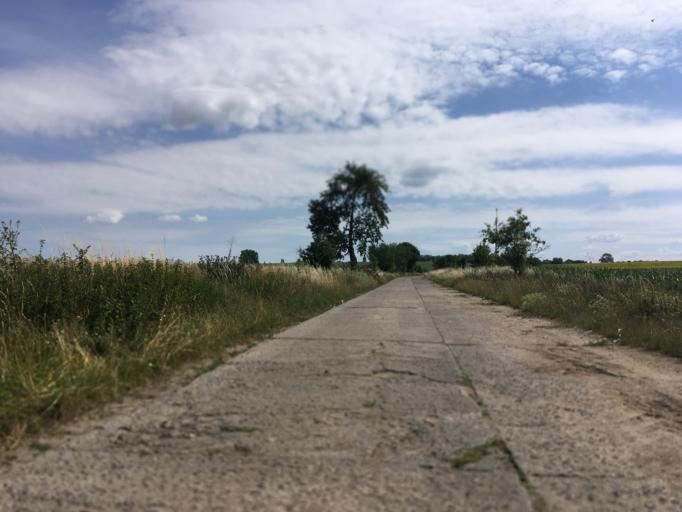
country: DE
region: Brandenburg
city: Passow
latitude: 53.2023
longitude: 14.1370
